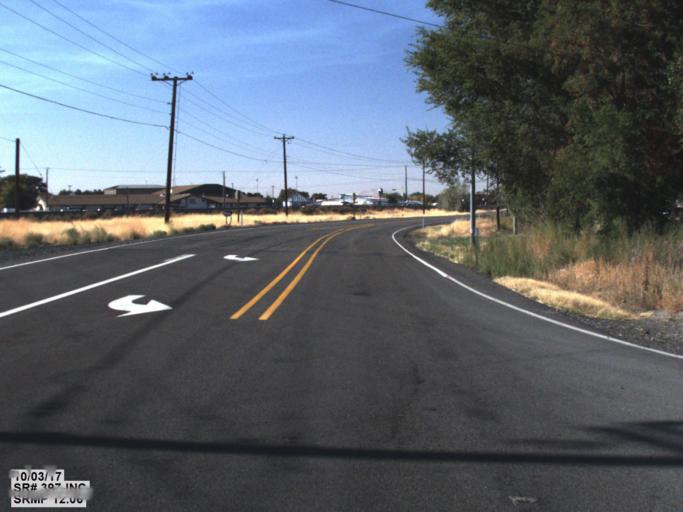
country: US
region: Washington
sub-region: Benton County
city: Finley
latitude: 46.1536
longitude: -119.0298
